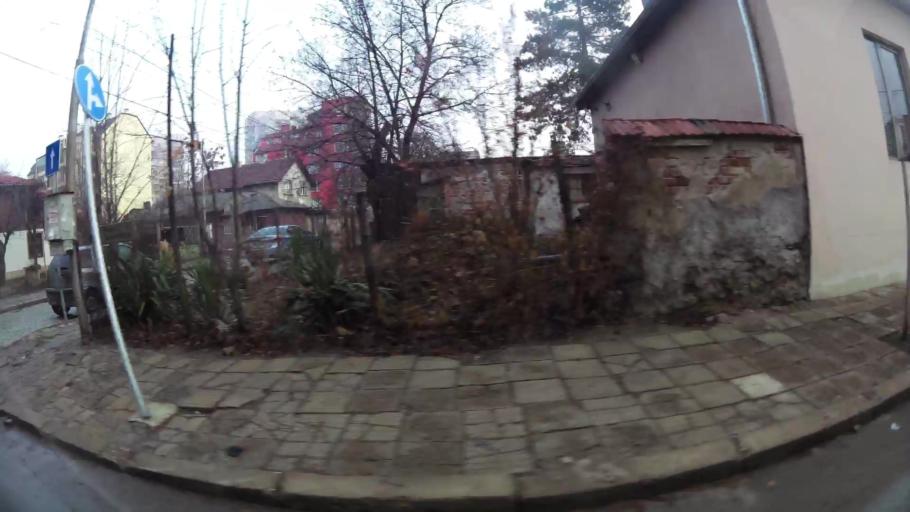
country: BG
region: Sofia-Capital
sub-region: Stolichna Obshtina
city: Sofia
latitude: 42.7280
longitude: 23.3030
